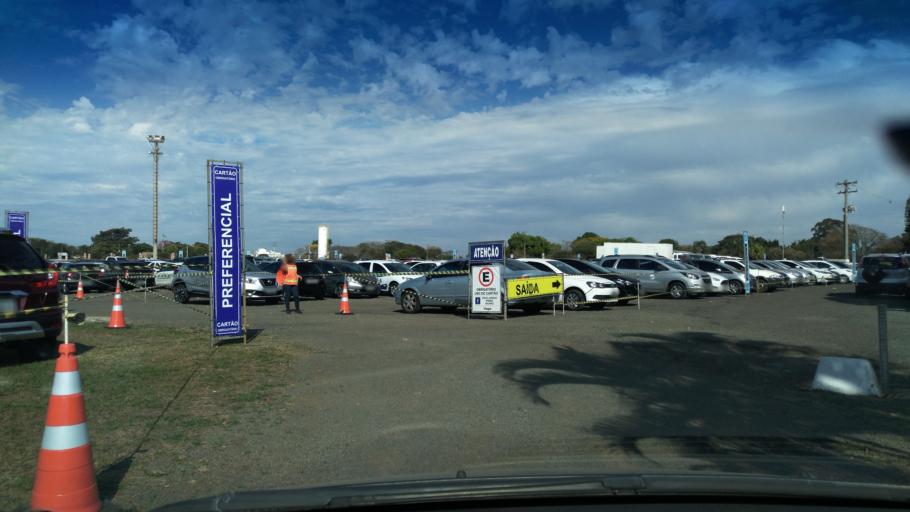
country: BR
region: Sao Paulo
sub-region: Jaguariuna
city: Jaguariuna
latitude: -22.6253
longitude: -47.0563
